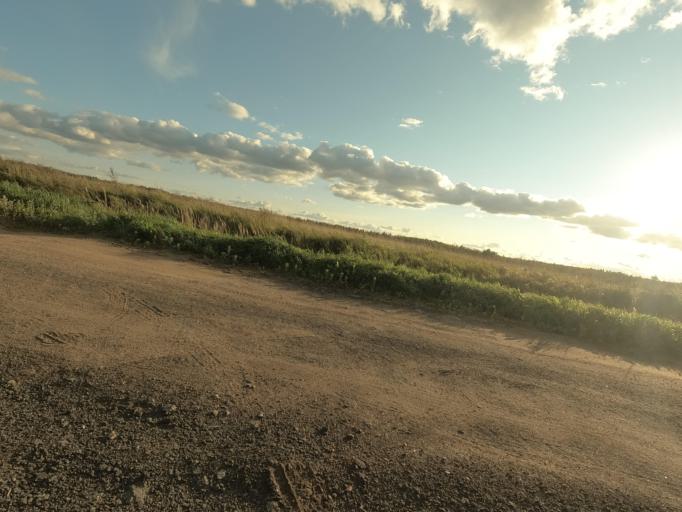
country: RU
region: Leningrad
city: Imeni Sverdlova
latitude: 59.8662
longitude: 30.7354
